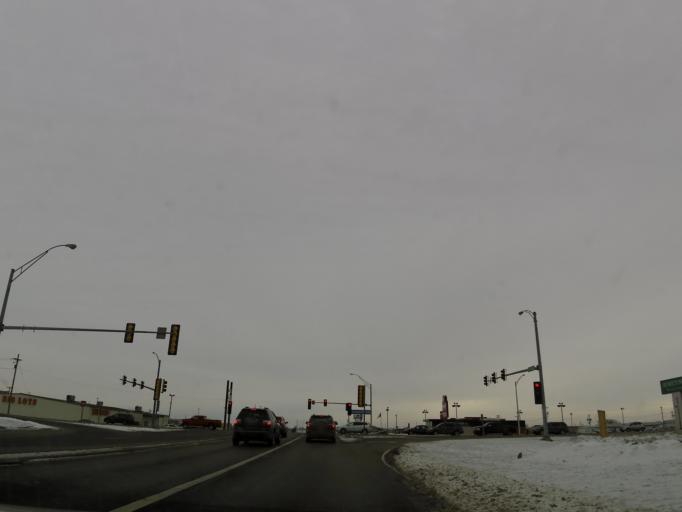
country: US
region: Illinois
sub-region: LaSalle County
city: Peru
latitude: 41.3586
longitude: -89.1264
